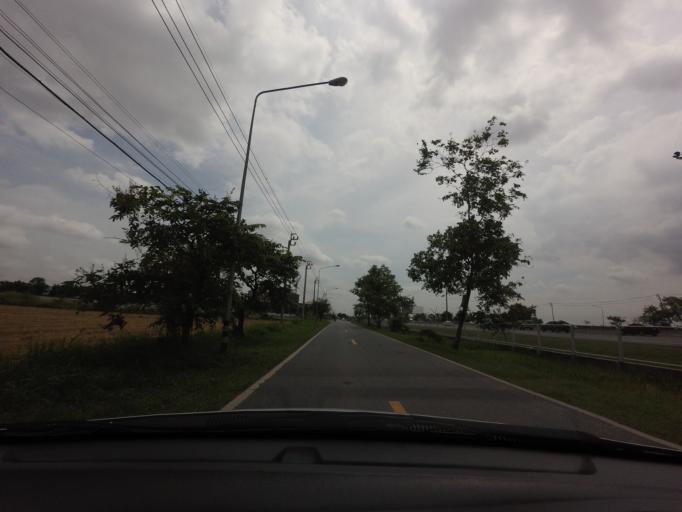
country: TH
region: Bangkok
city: Khan Na Yao
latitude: 13.8730
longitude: 100.6810
